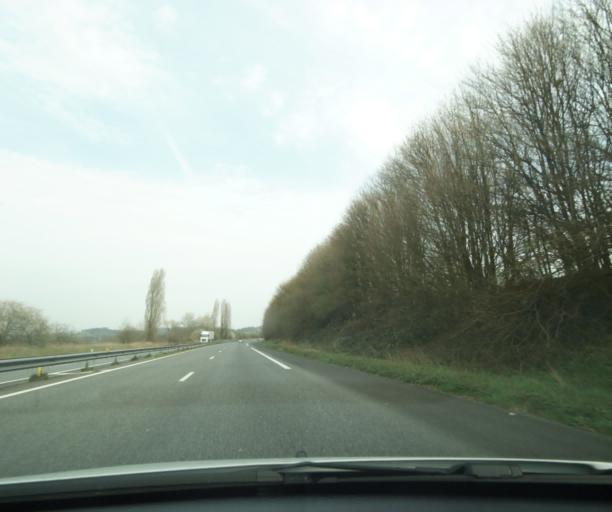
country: FR
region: Aquitaine
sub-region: Departement des Pyrenees-Atlantiques
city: Puyoo
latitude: 43.5072
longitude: -0.8516
